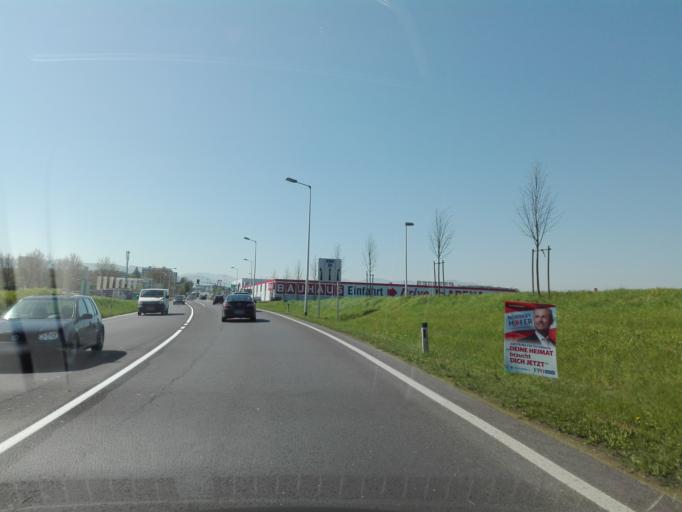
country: AT
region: Upper Austria
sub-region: Steyr Stadt
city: Steyr
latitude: 48.0659
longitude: 14.4212
